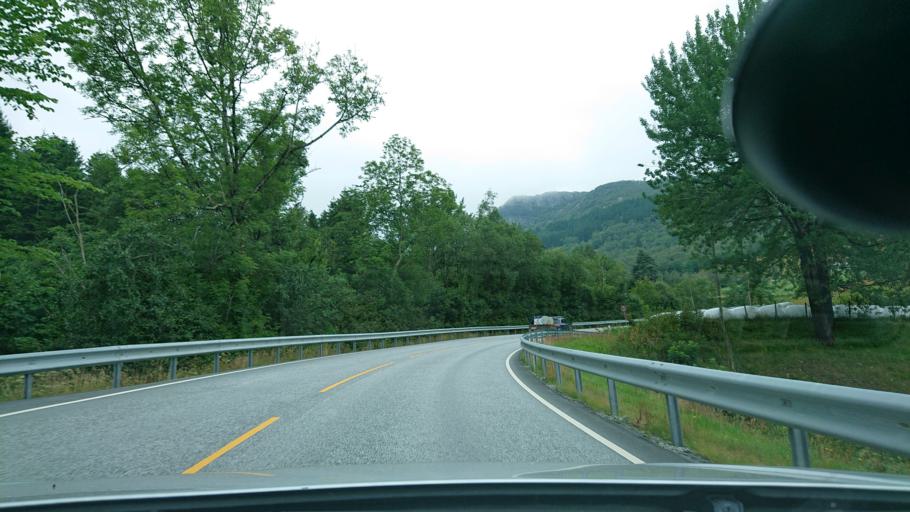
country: NO
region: Rogaland
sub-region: Hjelmeland
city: Hjelmelandsvagen
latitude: 59.1663
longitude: 6.1677
